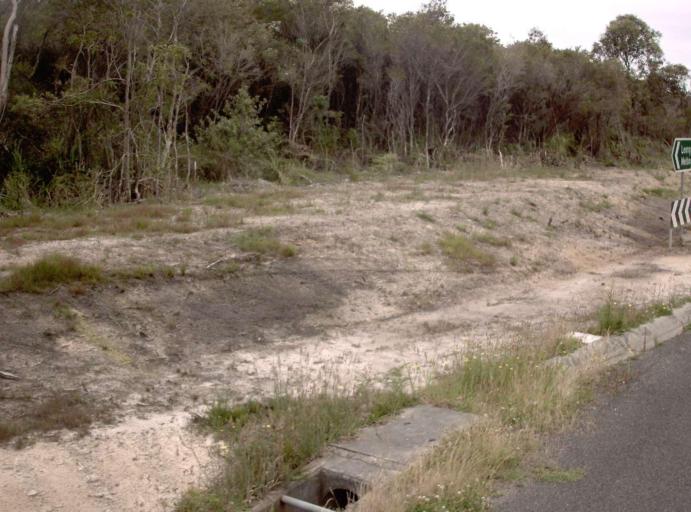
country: AU
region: Victoria
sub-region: Latrobe
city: Morwell
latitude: -38.6487
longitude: 146.2073
